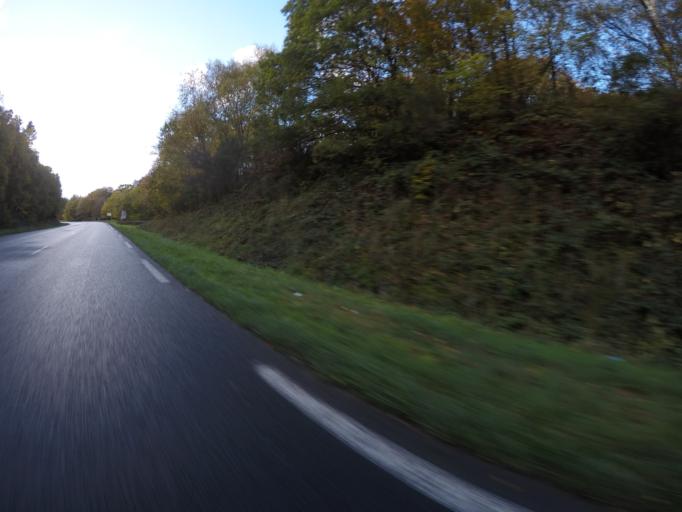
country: FR
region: Brittany
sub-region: Departement des Cotes-d'Armor
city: Guingamp
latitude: 48.5281
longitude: -3.1677
